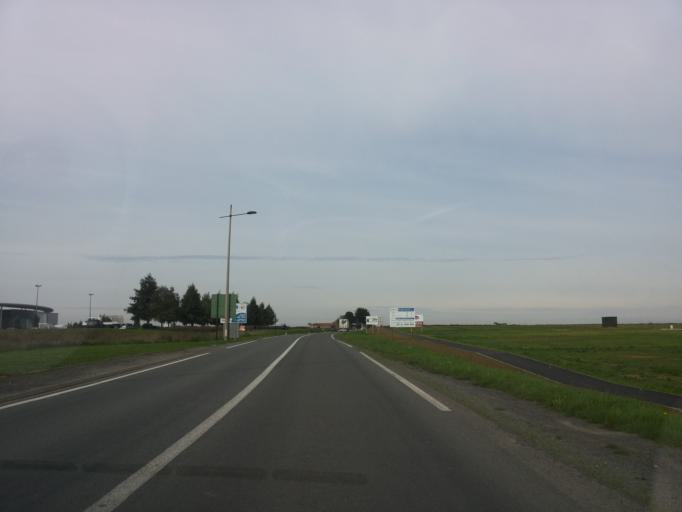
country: FR
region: Nord-Pas-de-Calais
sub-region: Departement du Pas-de-Calais
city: Marquion
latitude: 50.2162
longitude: 3.0667
